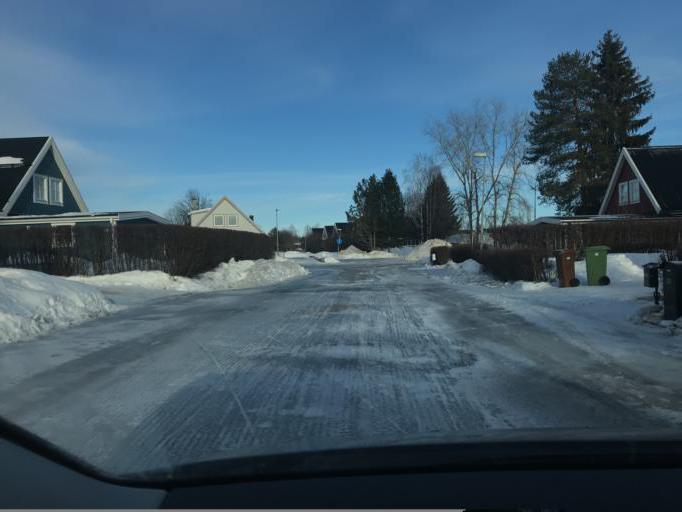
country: SE
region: Norrbotten
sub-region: Lulea Kommun
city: Sodra Sunderbyn
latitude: 65.6489
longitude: 21.9632
